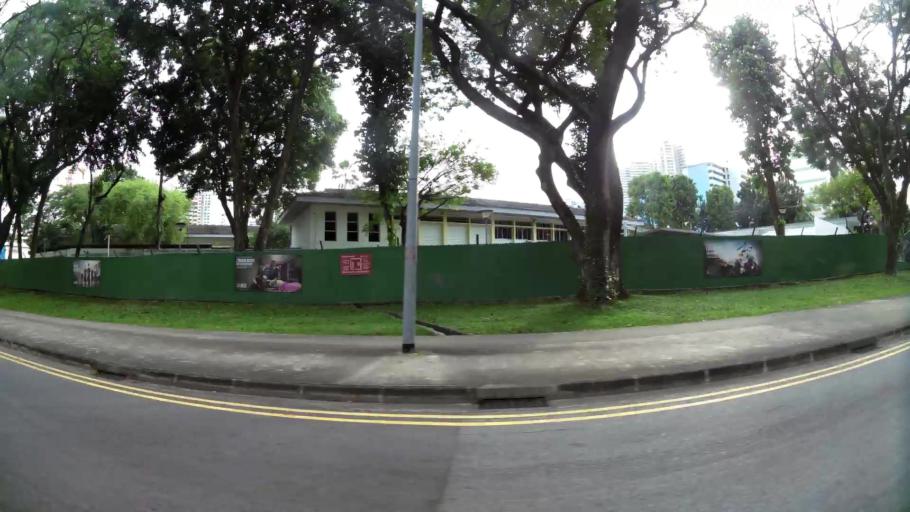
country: SG
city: Singapore
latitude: 1.3403
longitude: 103.8503
